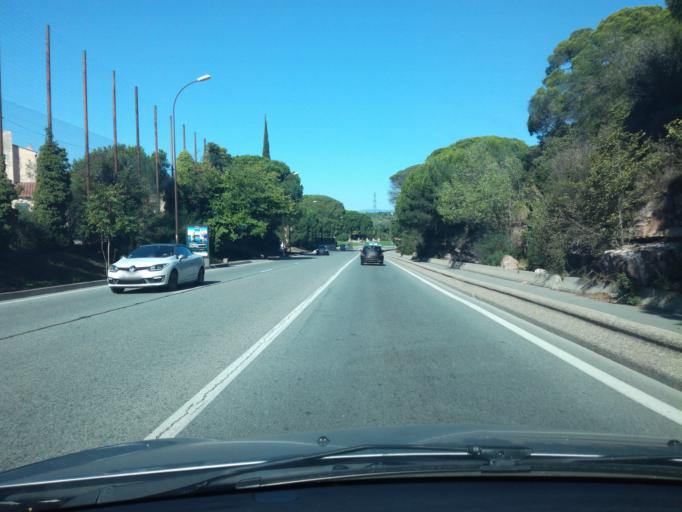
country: FR
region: Provence-Alpes-Cote d'Azur
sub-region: Departement du Var
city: Frejus
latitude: 43.4422
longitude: 6.7413
